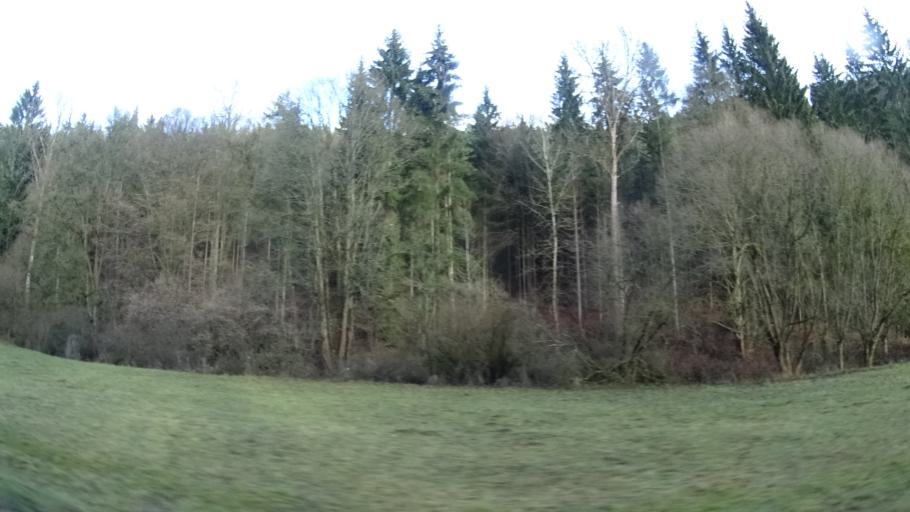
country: DE
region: Thuringia
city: Utendorf
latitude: 50.5945
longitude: 10.4455
